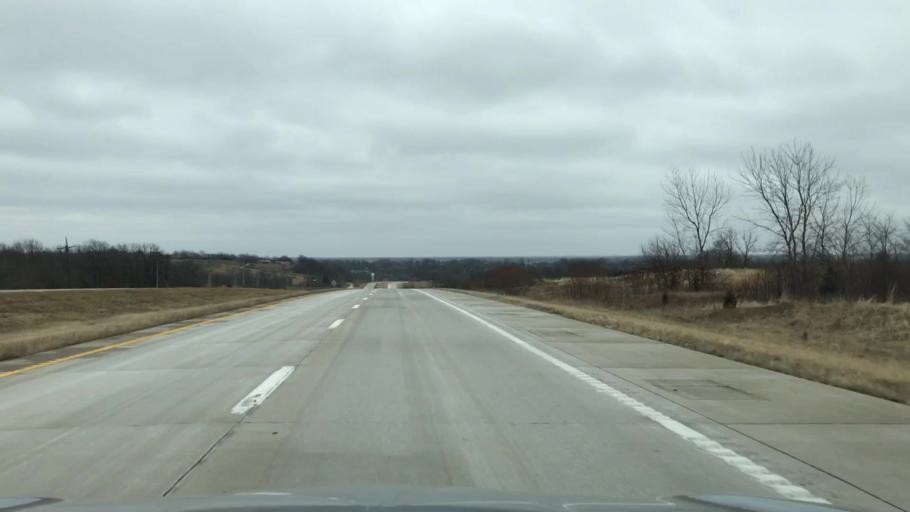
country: US
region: Missouri
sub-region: Livingston County
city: Chillicothe
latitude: 39.7395
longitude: -93.6570
